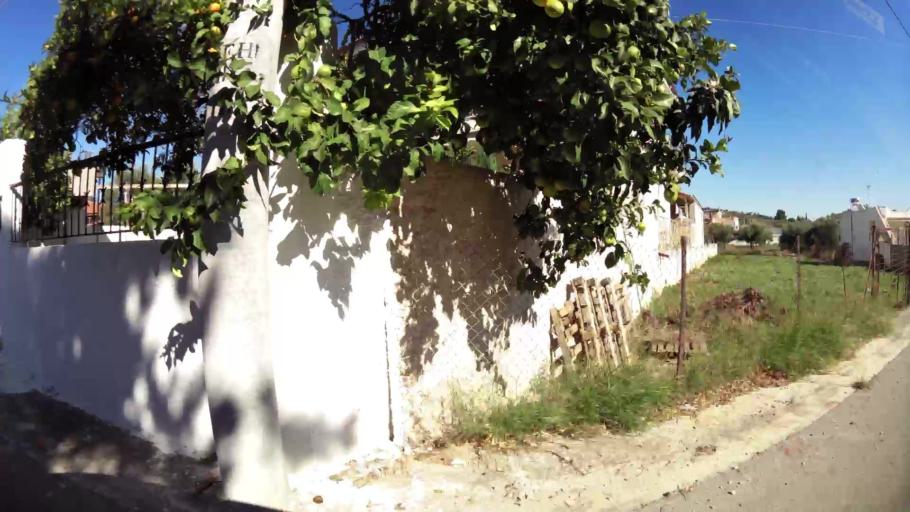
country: GR
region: Attica
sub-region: Nomarchia Anatolikis Attikis
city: Paiania
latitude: 37.9582
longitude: 23.8637
